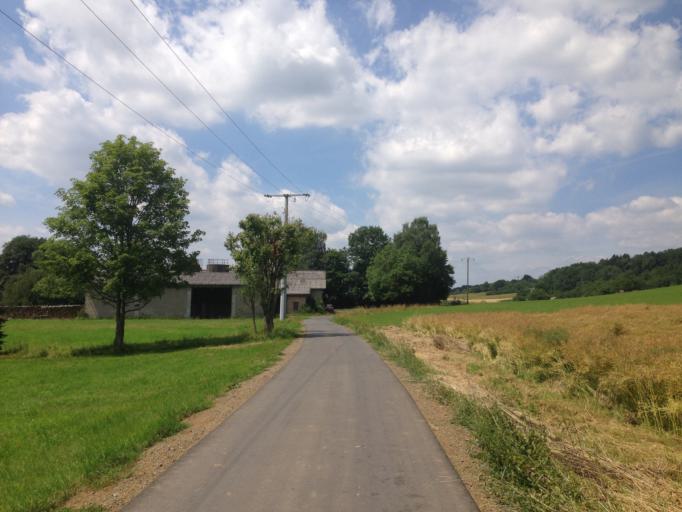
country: DE
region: Hesse
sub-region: Regierungsbezirk Giessen
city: Grunberg
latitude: 50.5999
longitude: 8.9146
